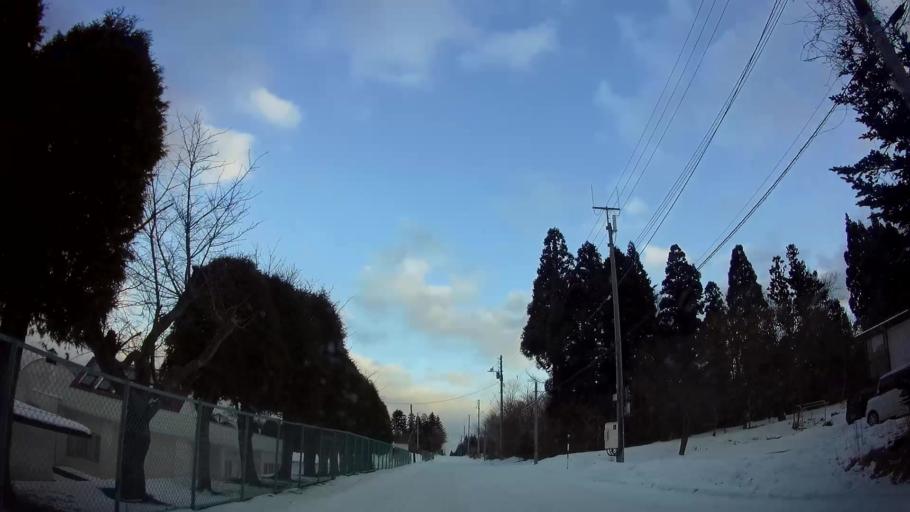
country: JP
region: Hokkaido
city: Nanae
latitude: 42.0225
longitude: 140.8338
